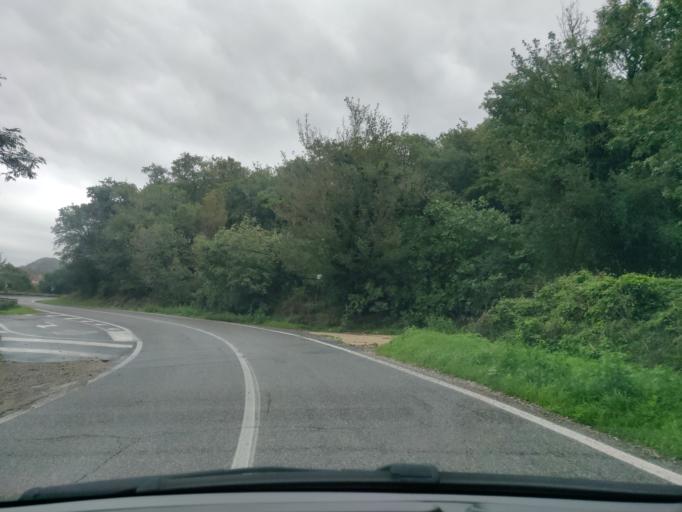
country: IT
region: Latium
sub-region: Citta metropolitana di Roma Capitale
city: Allumiere
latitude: 42.1440
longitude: 11.8866
